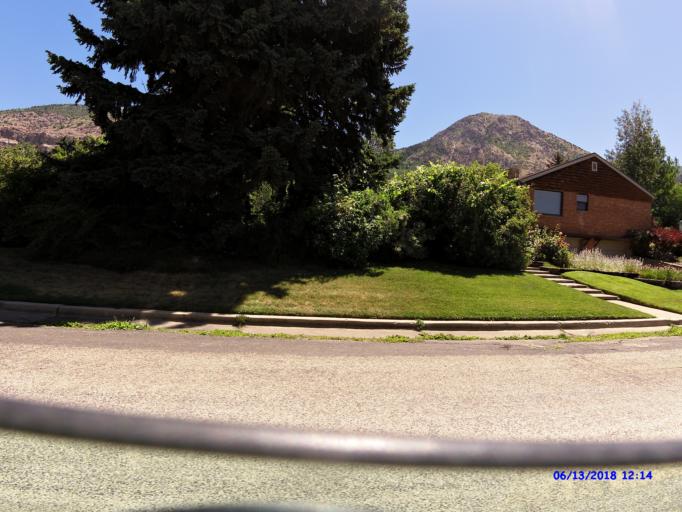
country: US
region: Utah
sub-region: Weber County
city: Ogden
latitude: 41.2148
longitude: -111.9361
